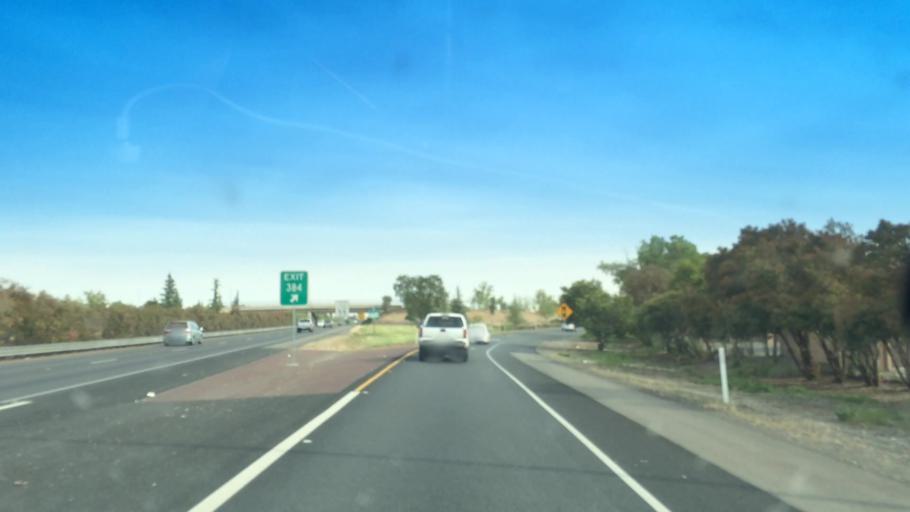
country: US
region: California
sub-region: Butte County
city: Chico
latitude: 39.7285
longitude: -121.8115
